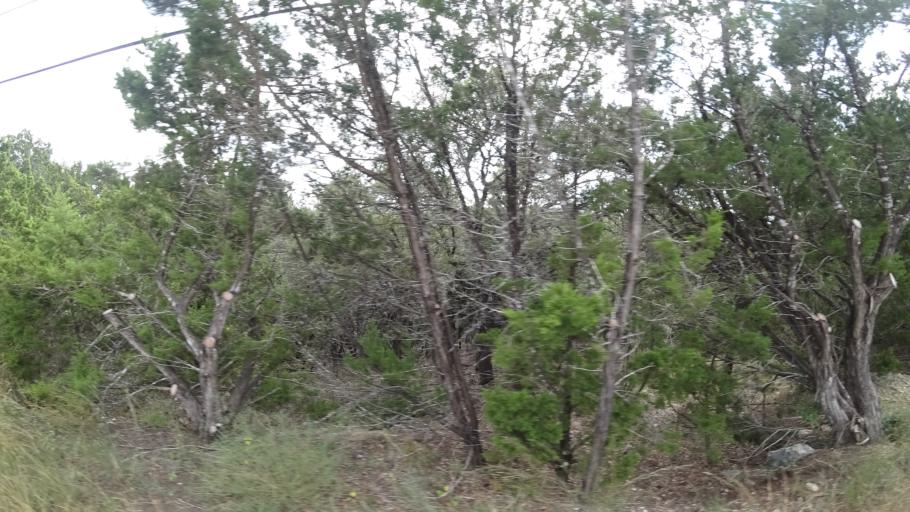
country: US
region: Texas
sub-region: Travis County
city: Hudson Bend
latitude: 30.3735
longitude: -97.9214
